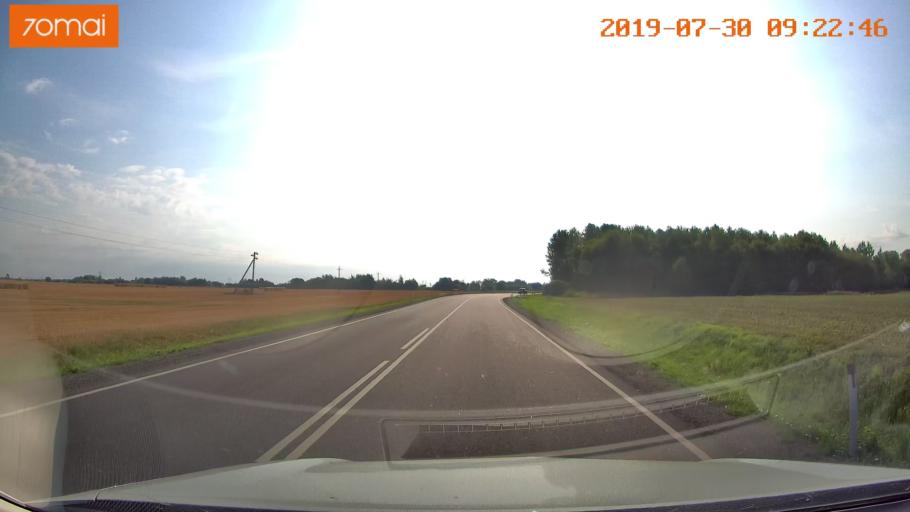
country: RU
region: Kaliningrad
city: Nesterov
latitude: 54.6341
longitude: 22.6607
